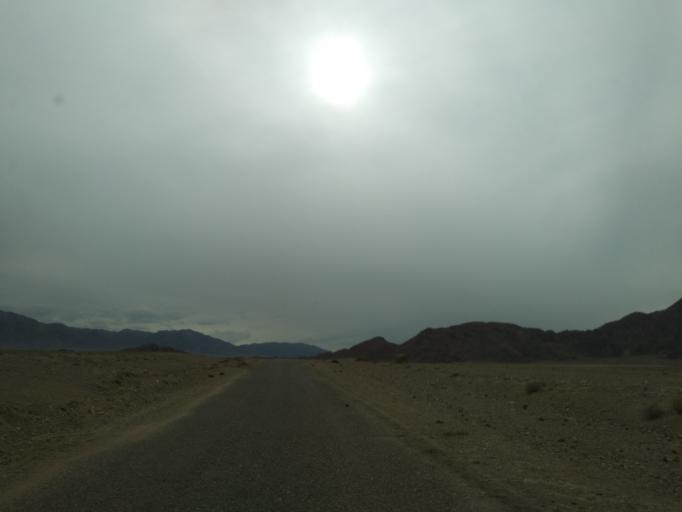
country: KG
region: Ysyk-Koel
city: Balykchy
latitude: 42.3178
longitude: 76.1628
